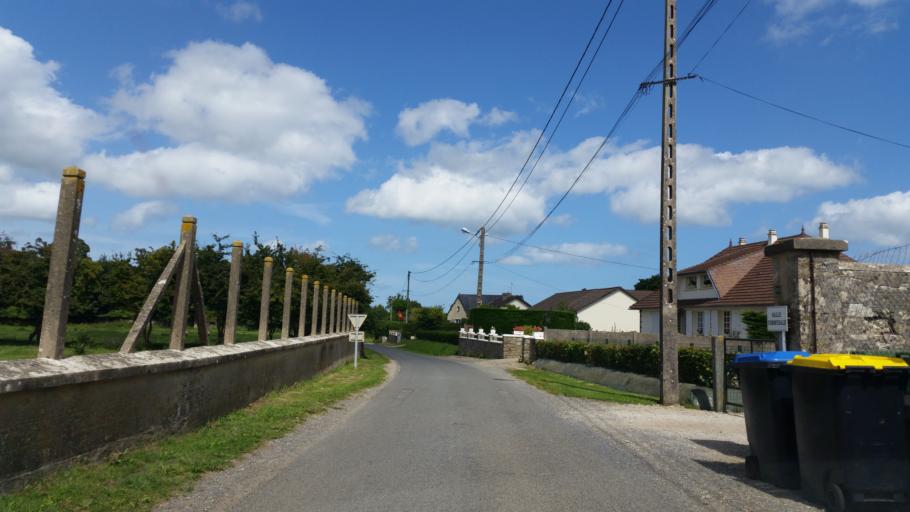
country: FR
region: Lower Normandy
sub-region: Departement de la Manche
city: Montebourg
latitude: 49.4597
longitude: -1.3418
